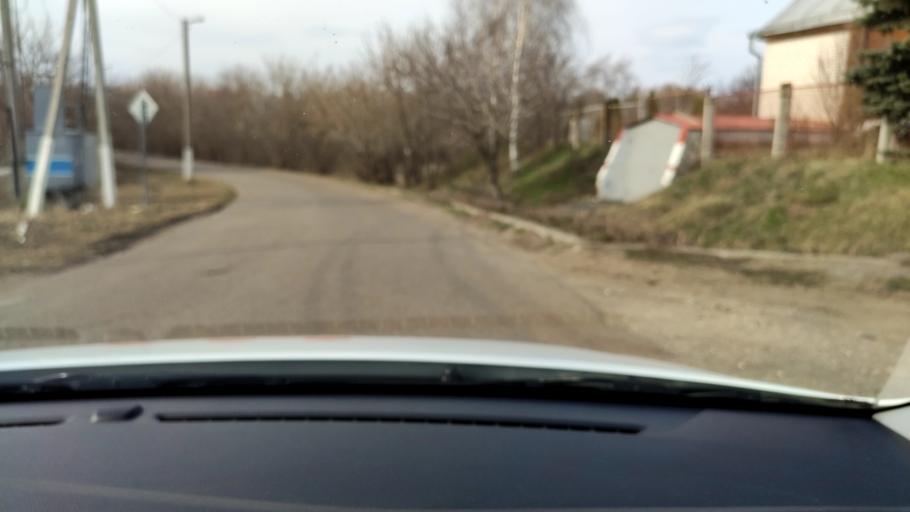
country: RU
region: Tatarstan
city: Stolbishchi
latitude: 55.6468
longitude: 49.3104
